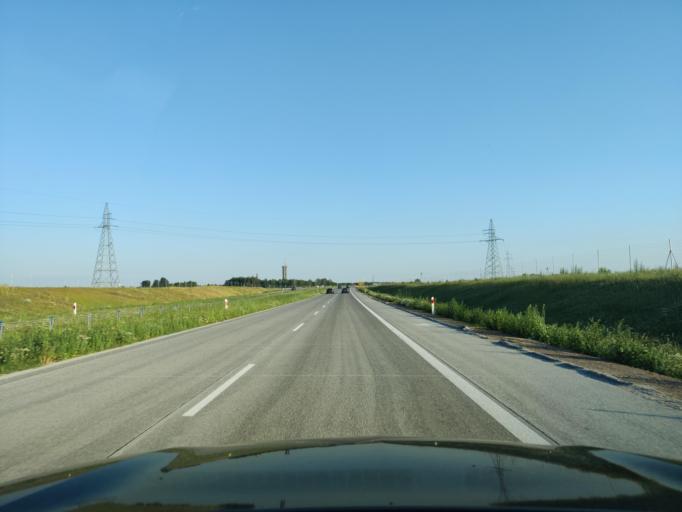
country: PL
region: Masovian Voivodeship
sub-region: Powiat mlawski
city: Mlawa
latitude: 53.1085
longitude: 20.4115
